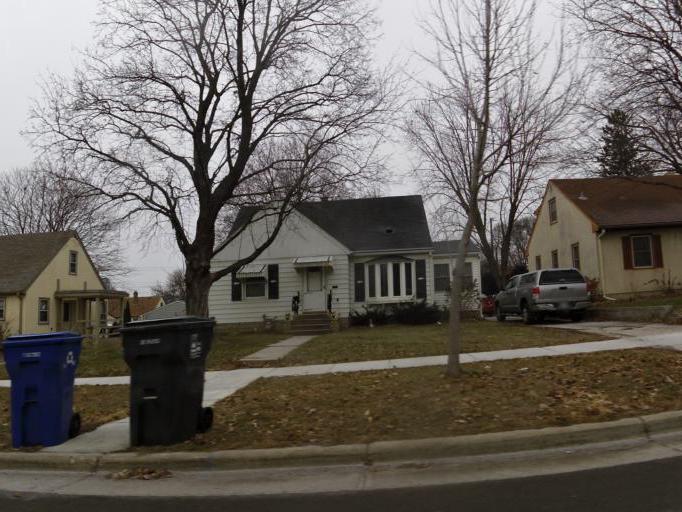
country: US
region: Minnesota
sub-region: Ramsey County
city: Maplewood
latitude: 44.9568
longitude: -93.0321
